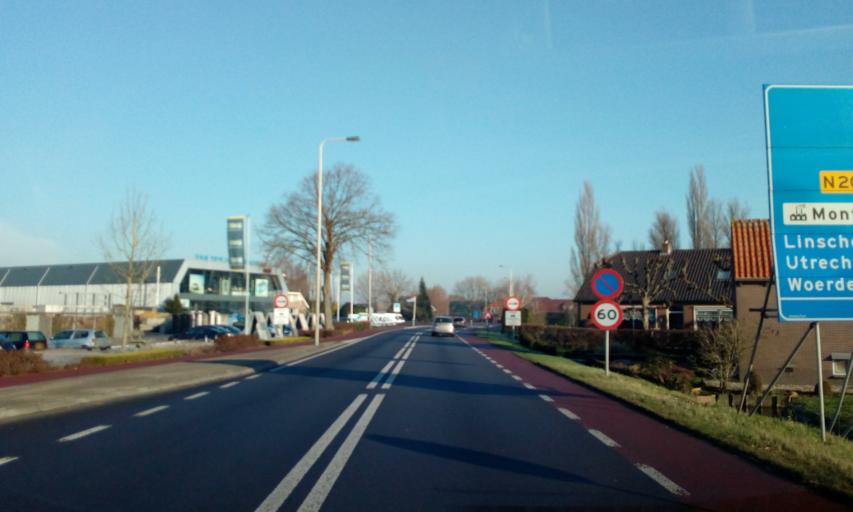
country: NL
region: Utrecht
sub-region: Gemeente Montfoort
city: Montfoort
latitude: 52.0327
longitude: 4.9333
